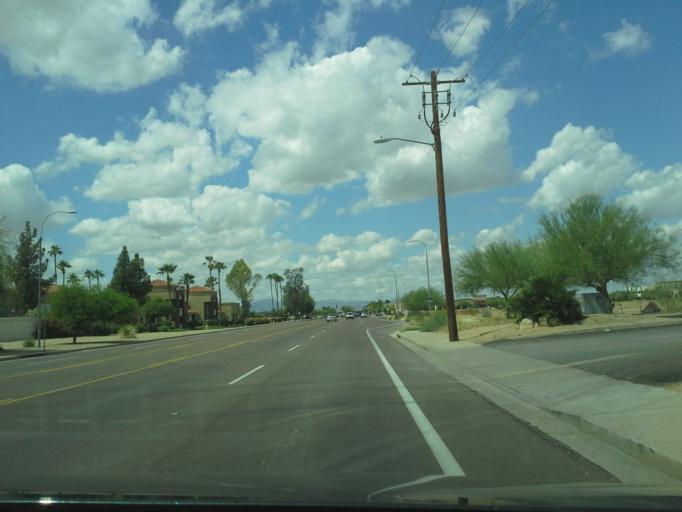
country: US
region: Arizona
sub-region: Maricopa County
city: Peoria
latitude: 33.6102
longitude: -112.2328
